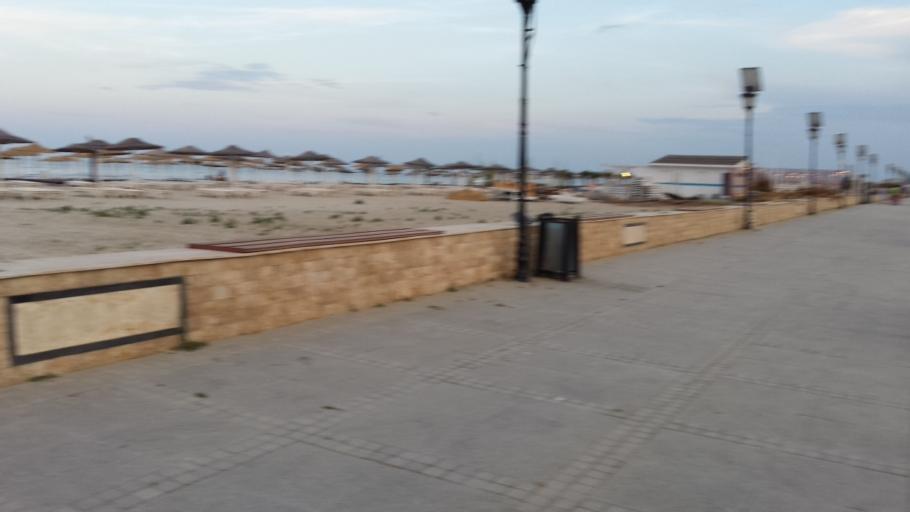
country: RO
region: Constanta
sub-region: Comuna Navodari
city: Navodari
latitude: 44.3214
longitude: 28.6362
